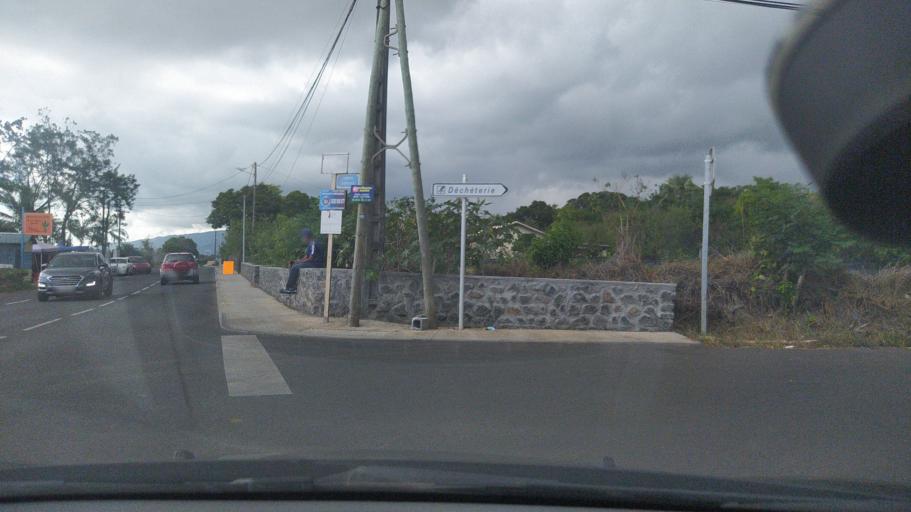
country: RE
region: Reunion
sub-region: Reunion
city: Saint-Pierre
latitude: -21.3060
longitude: 55.4640
